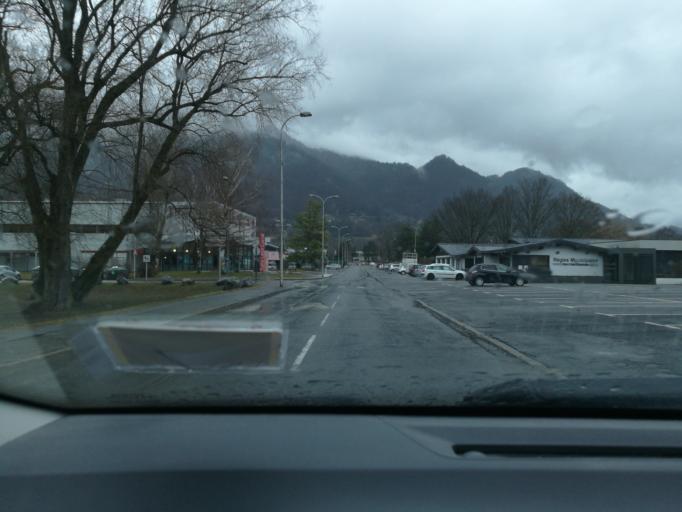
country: FR
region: Rhone-Alpes
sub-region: Departement de la Haute-Savoie
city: Sallanches
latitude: 45.9324
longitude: 6.6394
